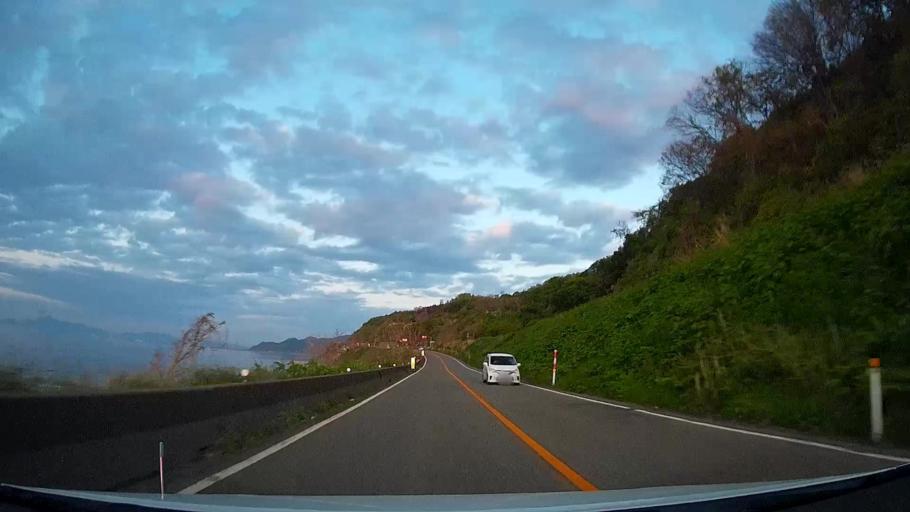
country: JP
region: Niigata
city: Joetsu
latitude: 37.1717
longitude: 138.1127
